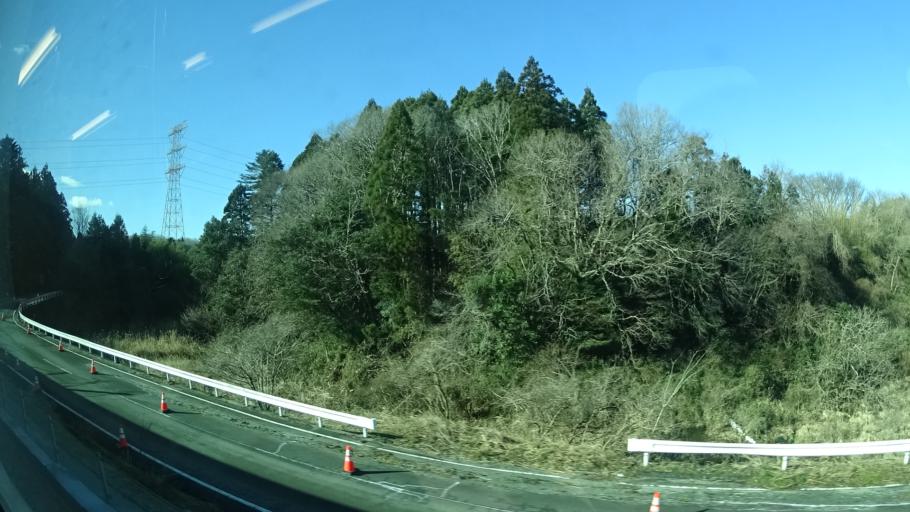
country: JP
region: Fukushima
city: Namie
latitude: 37.4294
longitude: 141.0014
